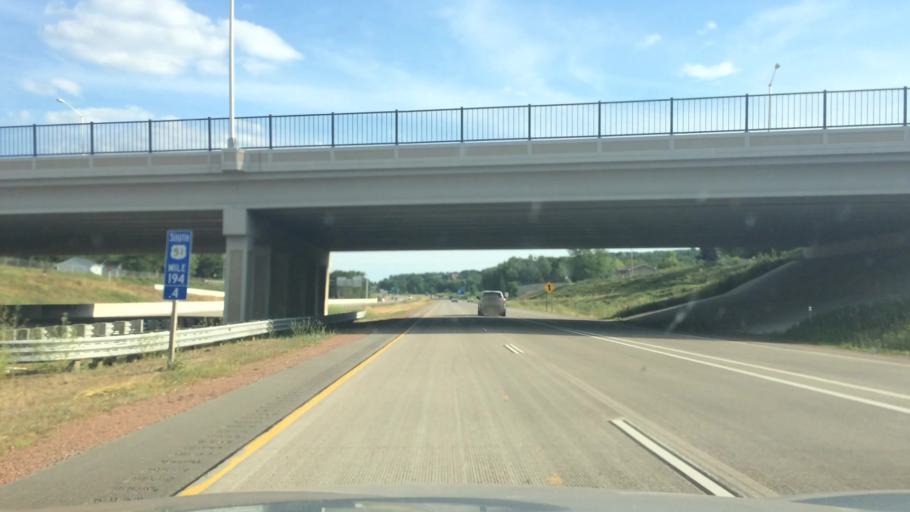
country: US
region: Wisconsin
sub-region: Marathon County
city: Wausau
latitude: 44.9867
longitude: -89.6567
